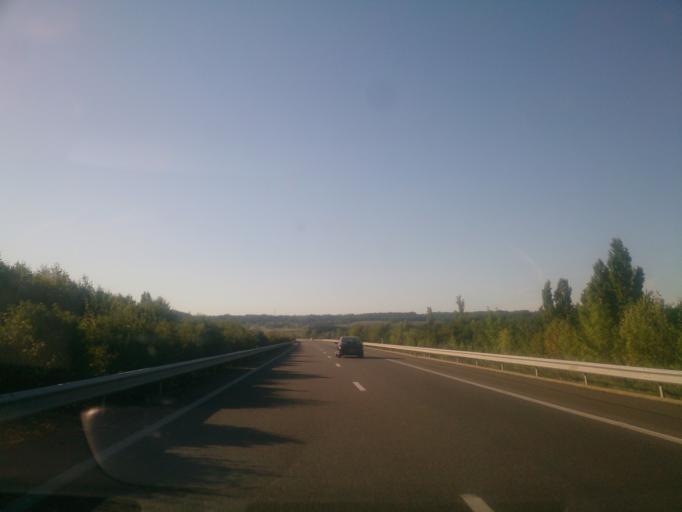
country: FR
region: Midi-Pyrenees
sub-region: Departement du Tarn-et-Garonne
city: Caussade
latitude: 44.2346
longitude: 1.5283
